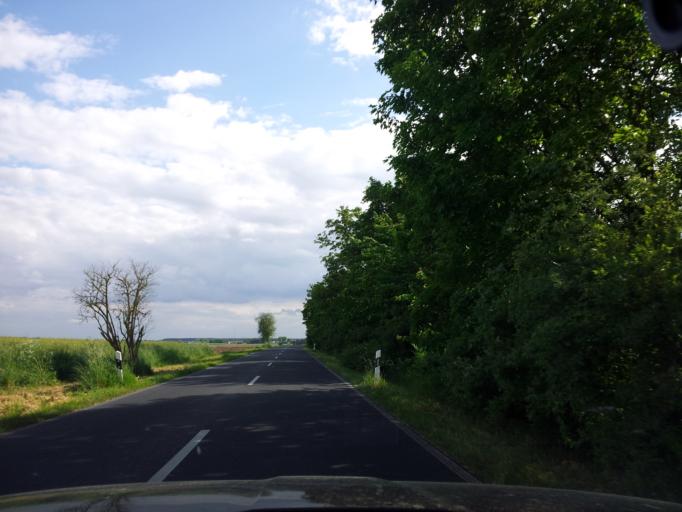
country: DE
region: Brandenburg
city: Niedergorsdorf
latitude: 51.9724
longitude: 12.9069
